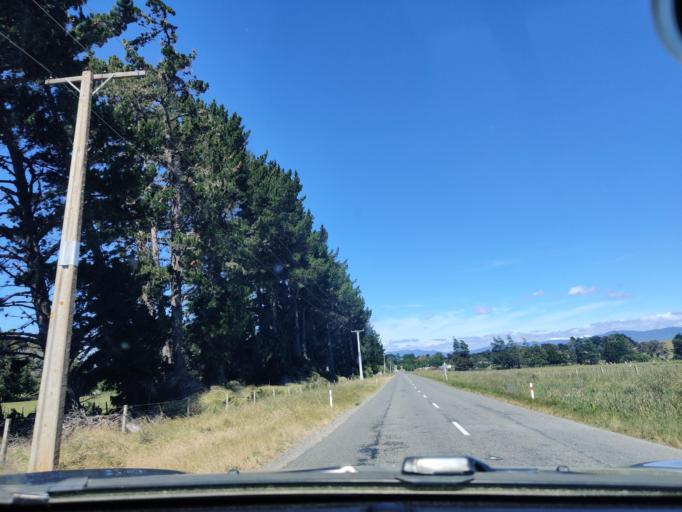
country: NZ
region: Wellington
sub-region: South Wairarapa District
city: Waipawa
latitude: -41.2251
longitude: 175.3511
